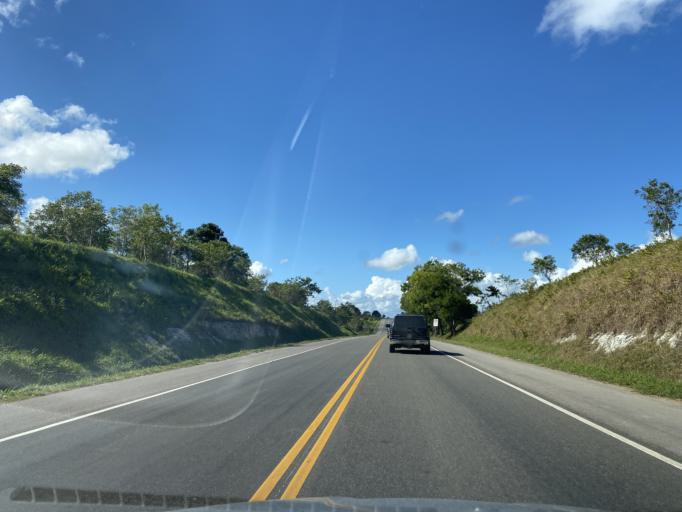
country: DO
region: Monte Plata
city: Sabana Grande de Boya
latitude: 18.9834
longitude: -69.8048
